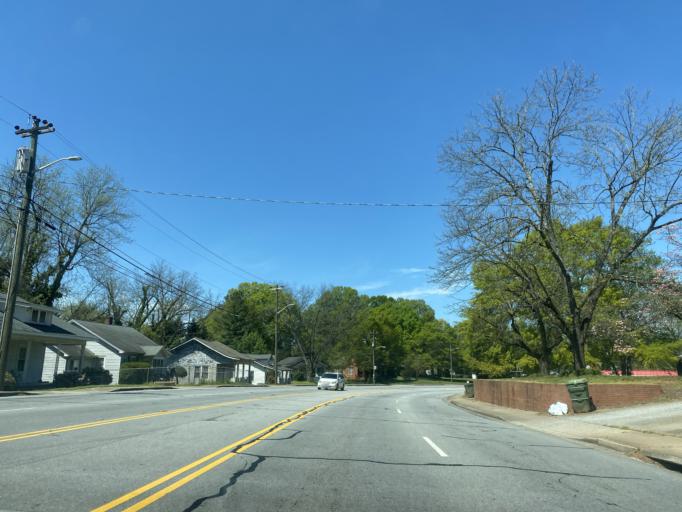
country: US
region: South Carolina
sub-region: Cherokee County
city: Gaffney
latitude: 35.0617
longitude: -81.6431
